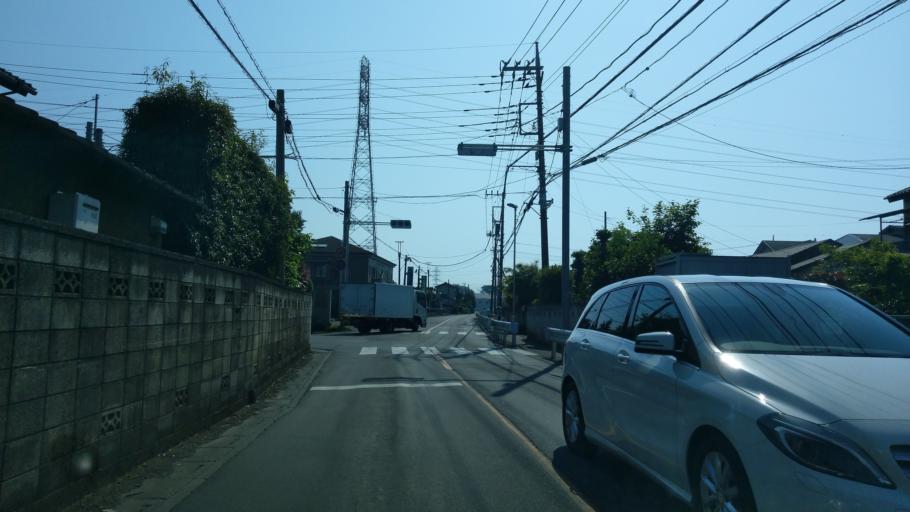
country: JP
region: Saitama
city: Oi
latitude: 35.8498
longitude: 139.5067
